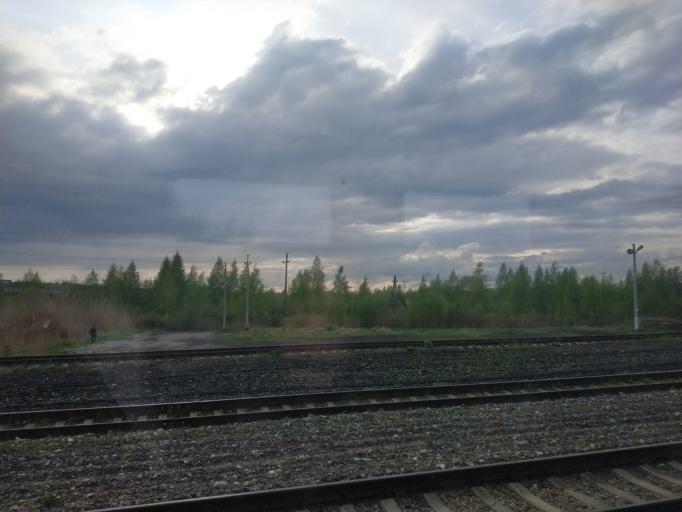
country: RU
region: Smolensk
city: Ugra
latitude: 54.7746
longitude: 34.3426
